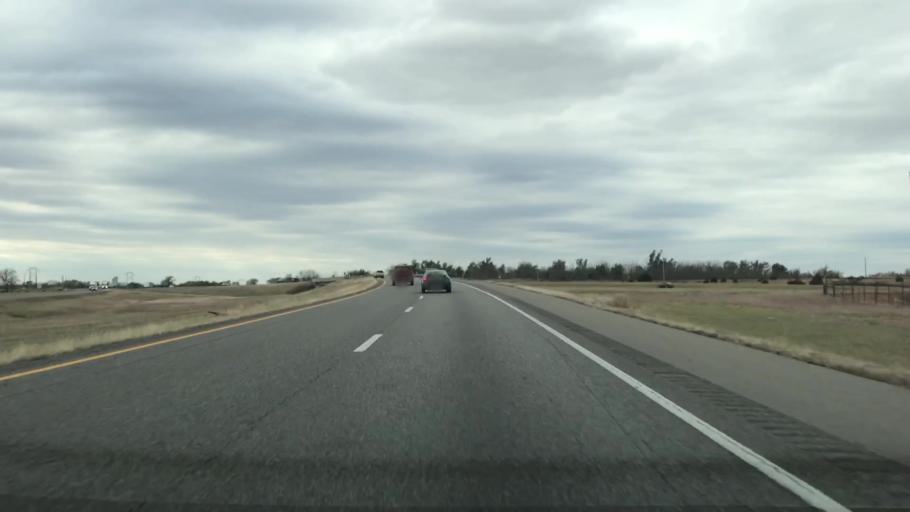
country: US
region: Oklahoma
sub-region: Beckham County
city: Elk City
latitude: 35.3858
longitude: -99.5091
